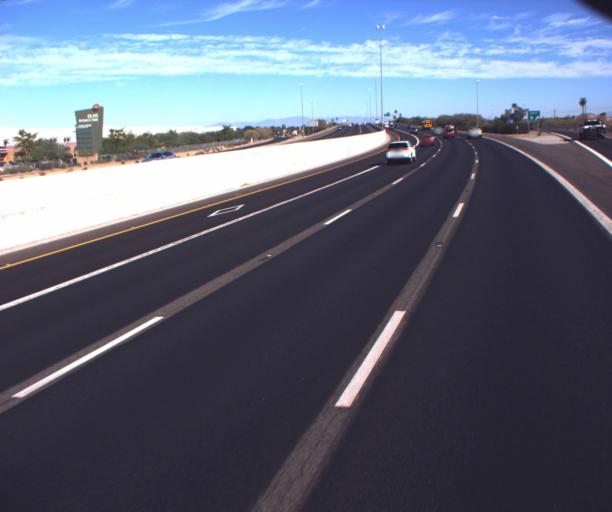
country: US
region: Arizona
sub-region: Maricopa County
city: Peoria
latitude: 33.5610
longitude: -112.2573
